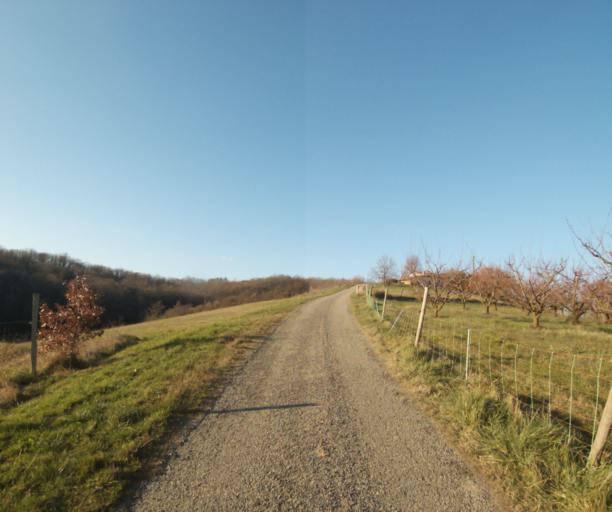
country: FR
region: Midi-Pyrenees
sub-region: Departement du Tarn-et-Garonne
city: Moissac
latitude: 44.1388
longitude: 1.1276
